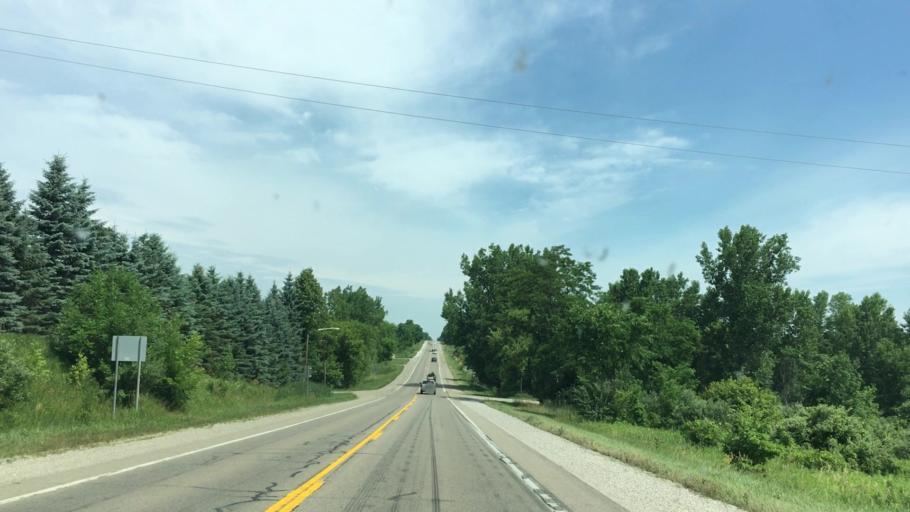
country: US
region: Michigan
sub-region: Lapeer County
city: Imlay City
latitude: 43.1083
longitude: -83.0723
